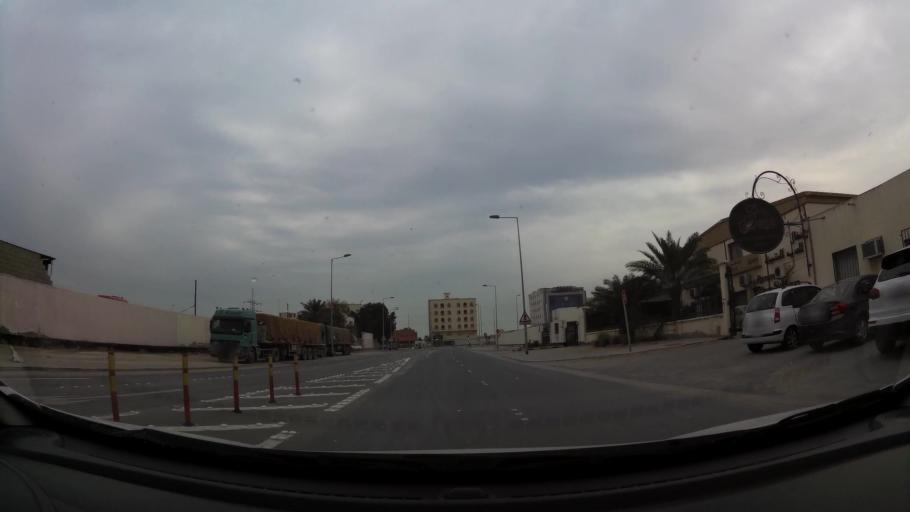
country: BH
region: Northern
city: Sitrah
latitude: 26.1772
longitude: 50.6037
